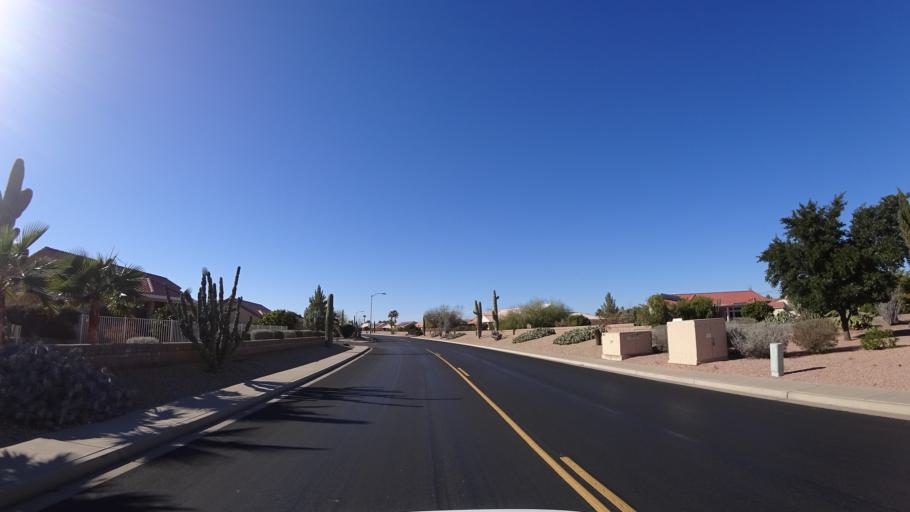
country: US
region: Arizona
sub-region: Maricopa County
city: Sun City West
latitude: 33.6934
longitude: -112.3708
